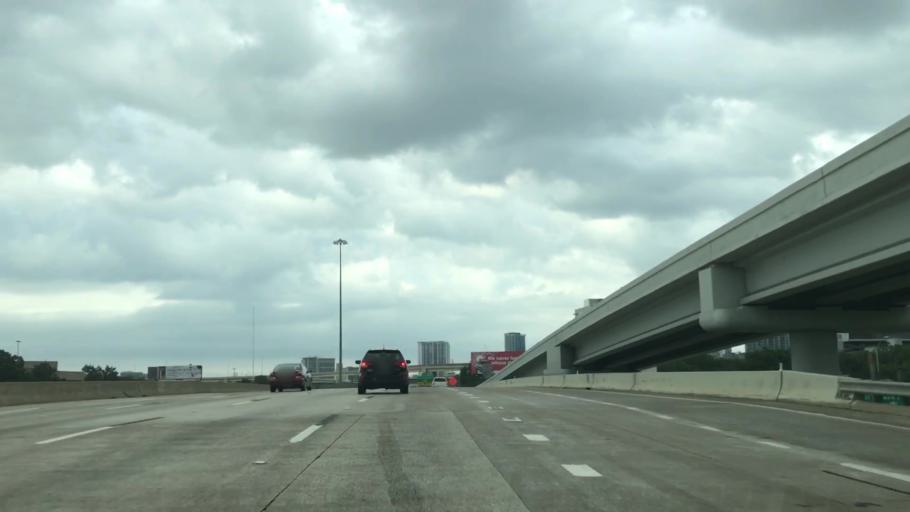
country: US
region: Texas
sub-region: Dallas County
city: Dallas
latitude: 32.7771
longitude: -96.8112
